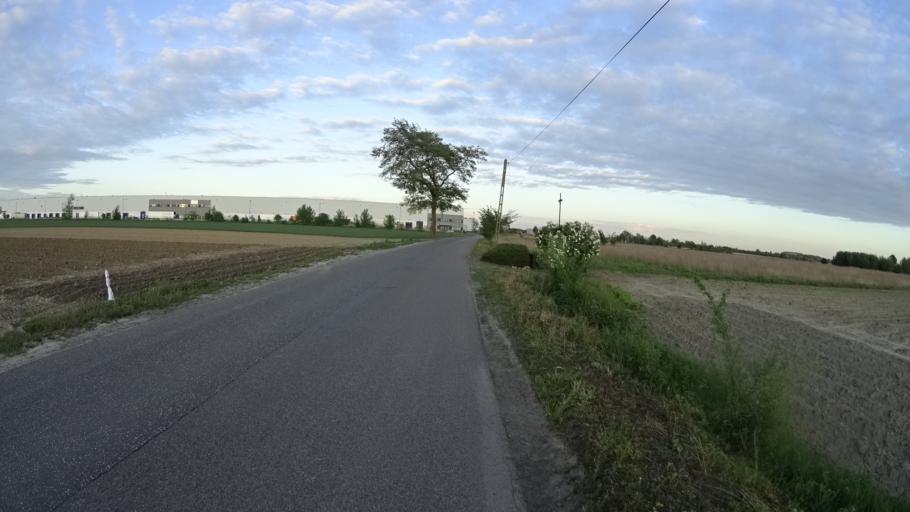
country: PL
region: Masovian Voivodeship
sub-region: Powiat warszawski zachodni
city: Ozarow Mazowiecki
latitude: 52.2029
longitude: 20.7619
